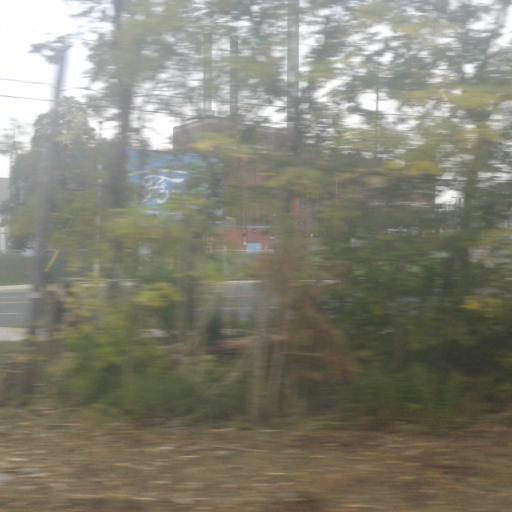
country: CA
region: Ontario
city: Windsor
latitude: 42.3241
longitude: -83.0002
